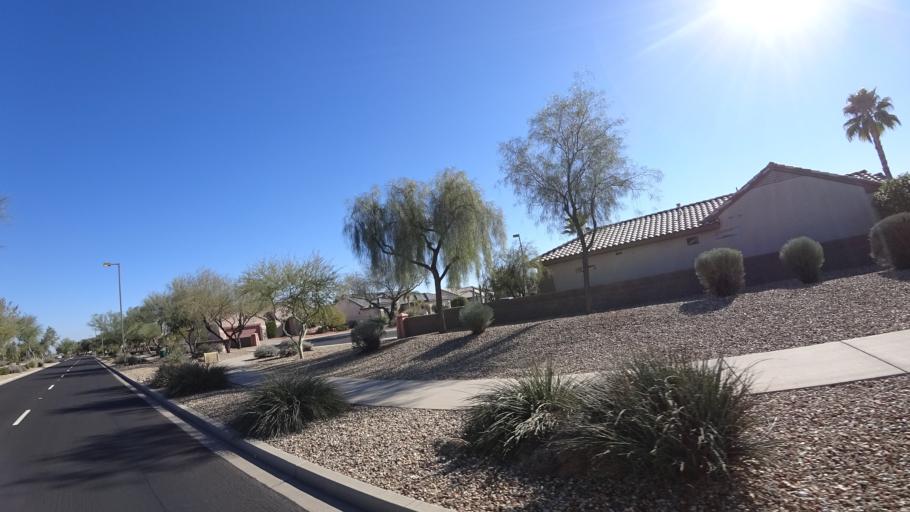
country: US
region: Arizona
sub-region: Maricopa County
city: Sun City West
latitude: 33.6556
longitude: -112.4088
